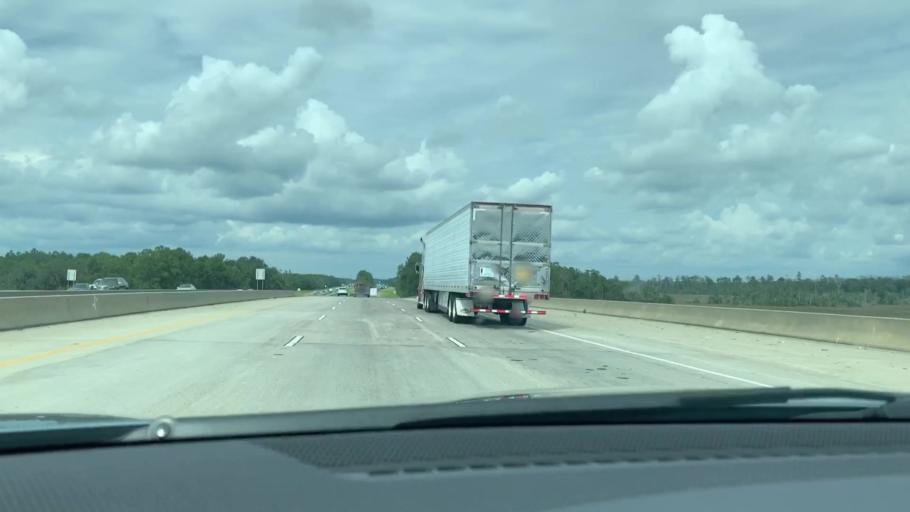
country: US
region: Georgia
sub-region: Liberty County
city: Midway
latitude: 31.7366
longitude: -81.3868
